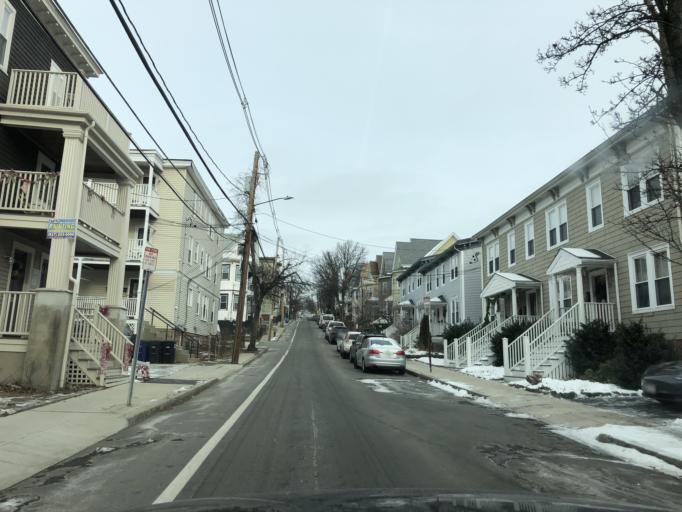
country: US
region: Massachusetts
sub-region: Middlesex County
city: Cambridge
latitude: 42.3856
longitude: -71.1112
